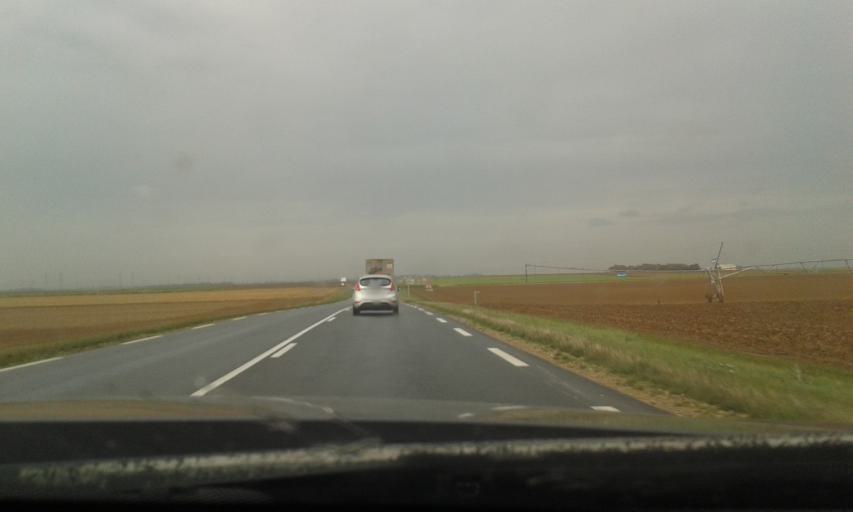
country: FR
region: Centre
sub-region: Departement d'Eure-et-Loir
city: Janville
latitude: 48.2356
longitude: 1.7867
